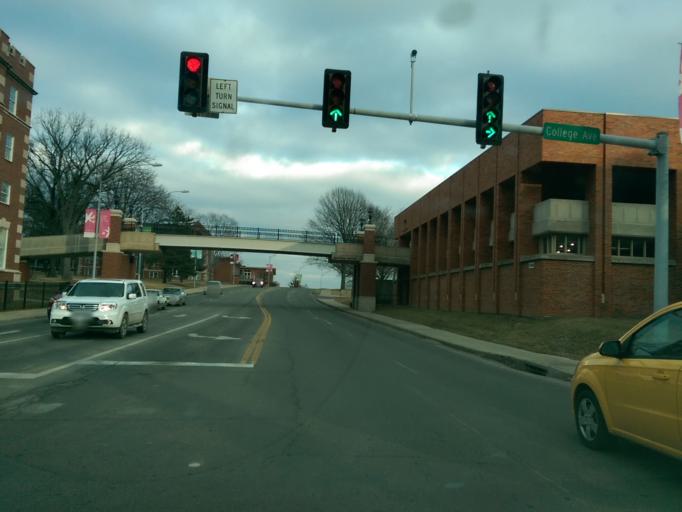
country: US
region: Missouri
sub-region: Boone County
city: Columbia
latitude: 38.9514
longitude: -92.3218
